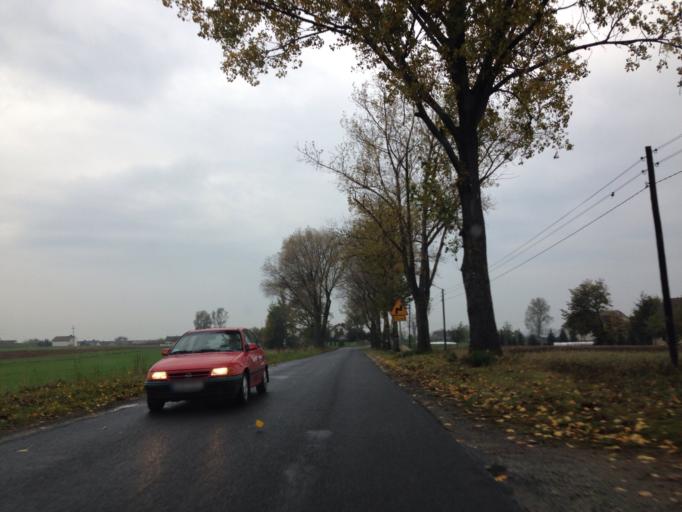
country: PL
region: Kujawsko-Pomorskie
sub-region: Powiat brodnicki
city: Swiedziebnia
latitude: 53.1611
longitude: 19.5305
